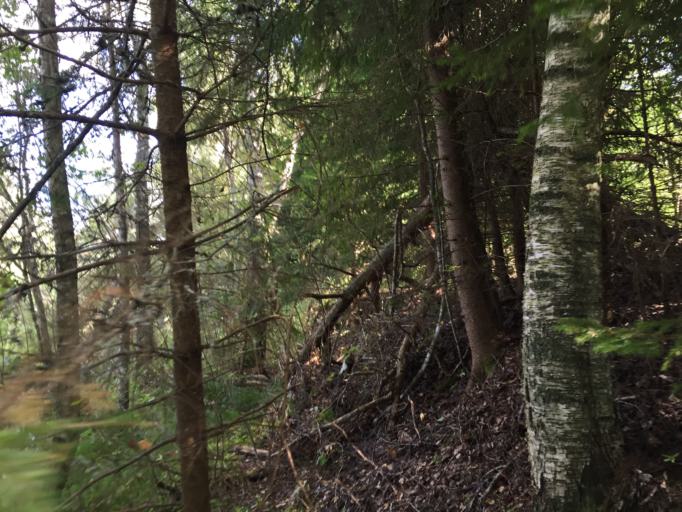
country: LV
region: Kuldigas Rajons
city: Kuldiga
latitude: 57.0026
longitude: 21.7953
